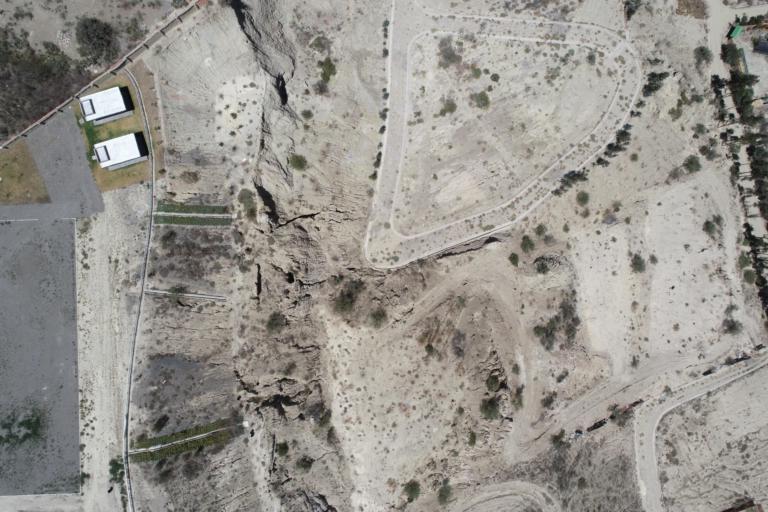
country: BO
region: La Paz
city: La Paz
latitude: -16.6209
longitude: -68.0594
